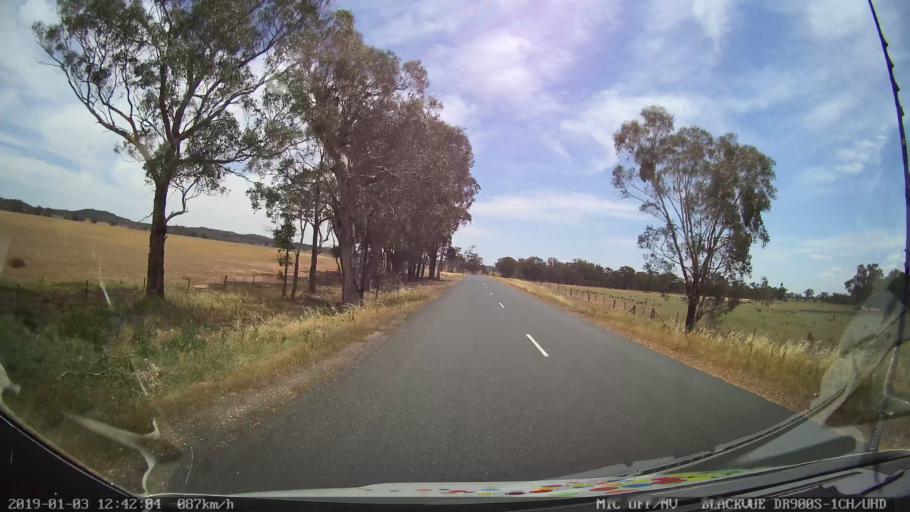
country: AU
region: New South Wales
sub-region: Weddin
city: Grenfell
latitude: -33.7916
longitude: 148.2138
